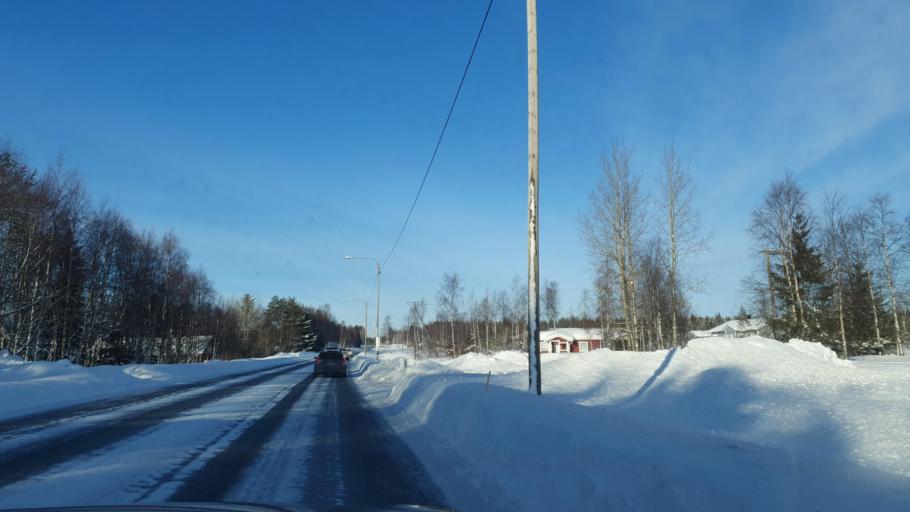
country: FI
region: Lapland
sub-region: Kemi-Tornio
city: Tornio
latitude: 65.9456
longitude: 24.0785
